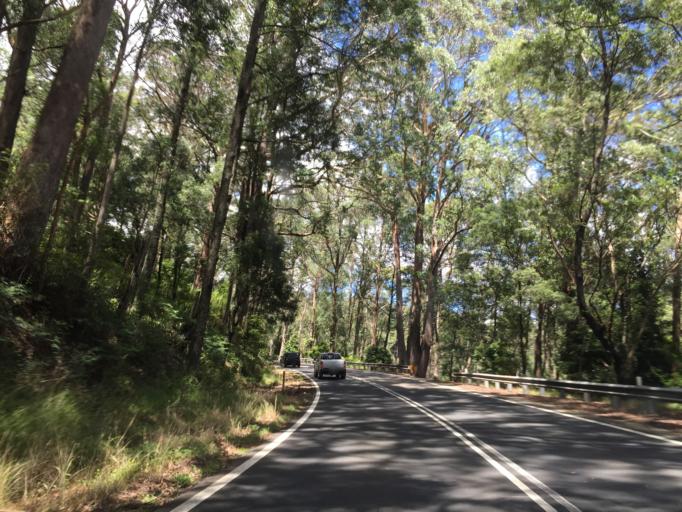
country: AU
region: New South Wales
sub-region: Blue Mountains Municipality
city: Blackheath
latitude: -33.5381
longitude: 150.4192
